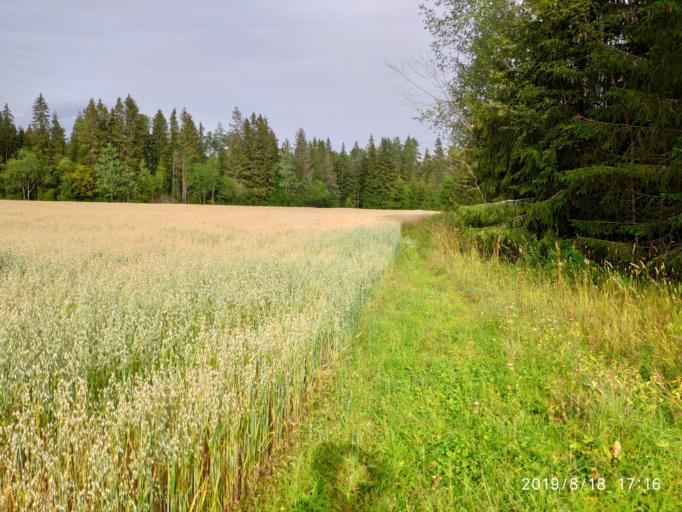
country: NO
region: Akershus
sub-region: Ullensaker
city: Jessheim
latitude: 60.1900
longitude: 11.2212
